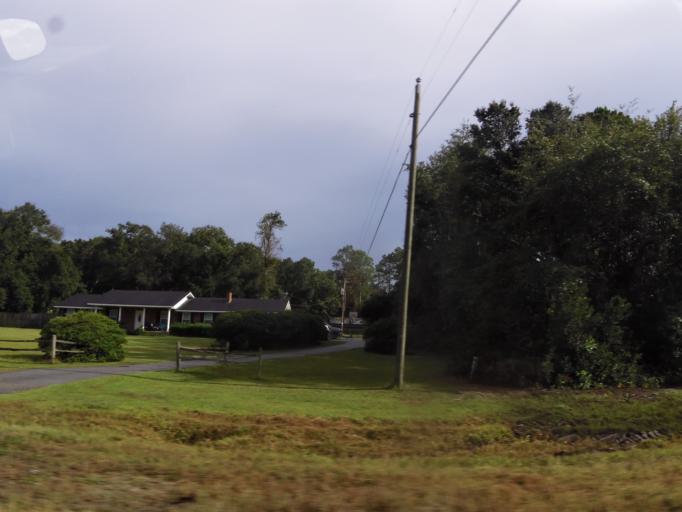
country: US
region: Georgia
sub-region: Liberty County
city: Walthourville
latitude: 31.7619
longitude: -81.6545
